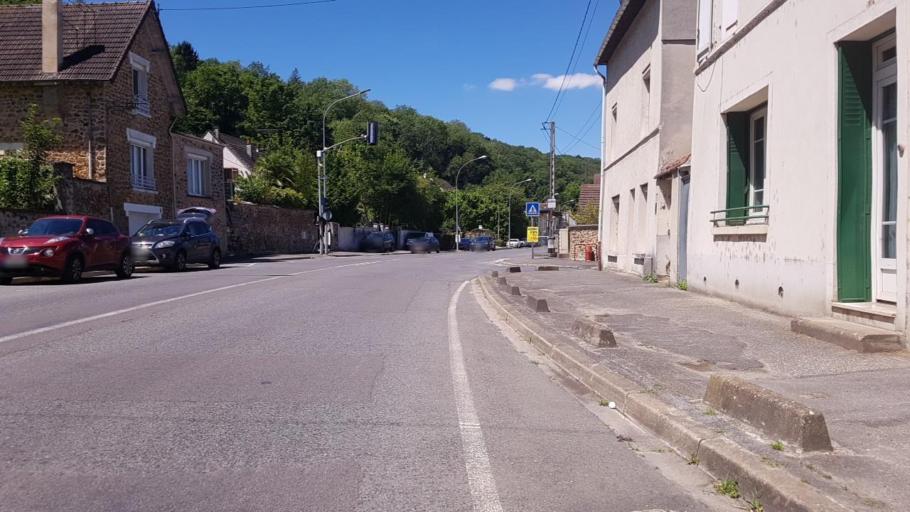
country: FR
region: Ile-de-France
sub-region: Departement de Seine-et-Marne
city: Saint-Jean-les-Deux-Jumeaux
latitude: 48.9521
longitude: 3.0129
